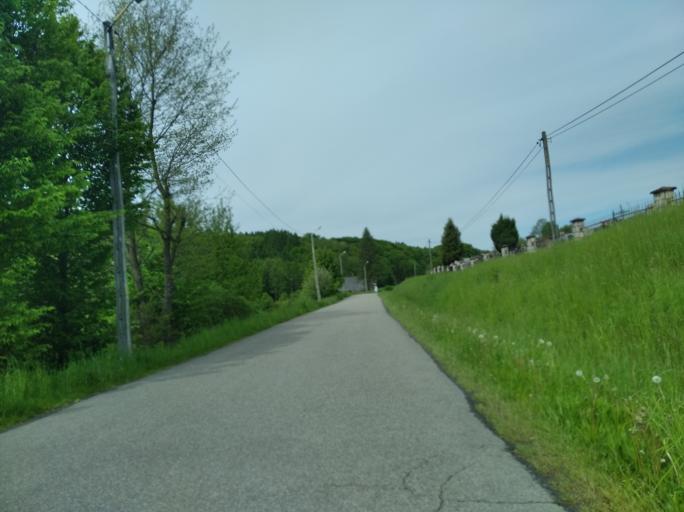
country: PL
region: Subcarpathian Voivodeship
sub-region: Powiat strzyzowski
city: Strzyzow
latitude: 49.9325
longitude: 21.7589
